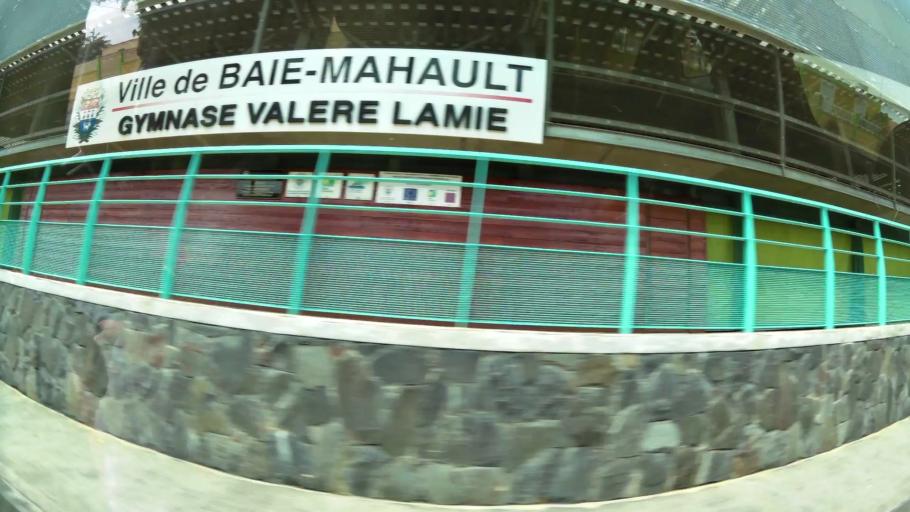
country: GP
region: Guadeloupe
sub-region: Guadeloupe
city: Baie-Mahault
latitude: 16.2644
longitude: -61.5889
